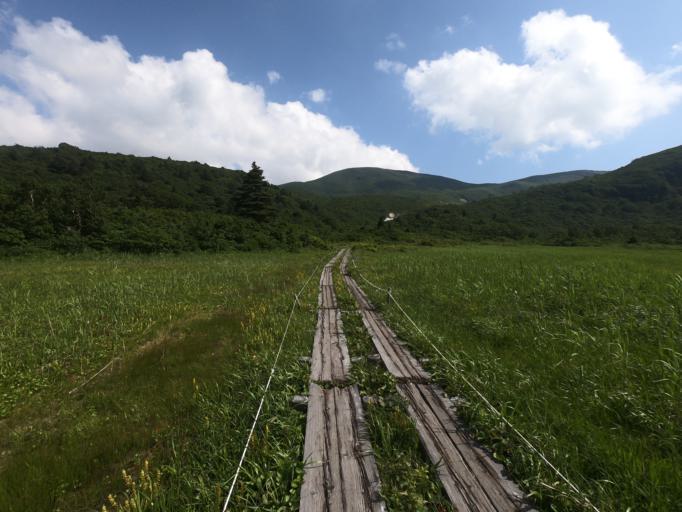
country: JP
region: Akita
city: Yuzawa
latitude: 38.9767
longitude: 140.7774
